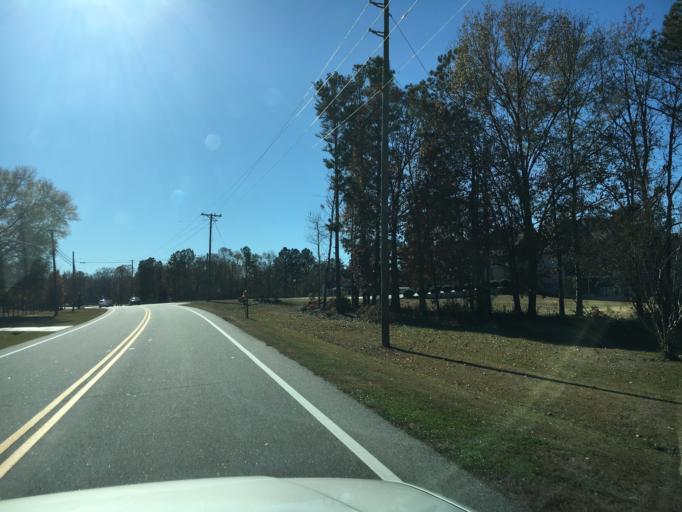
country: US
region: Georgia
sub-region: Hart County
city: Hartwell
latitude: 34.3073
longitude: -83.0010
